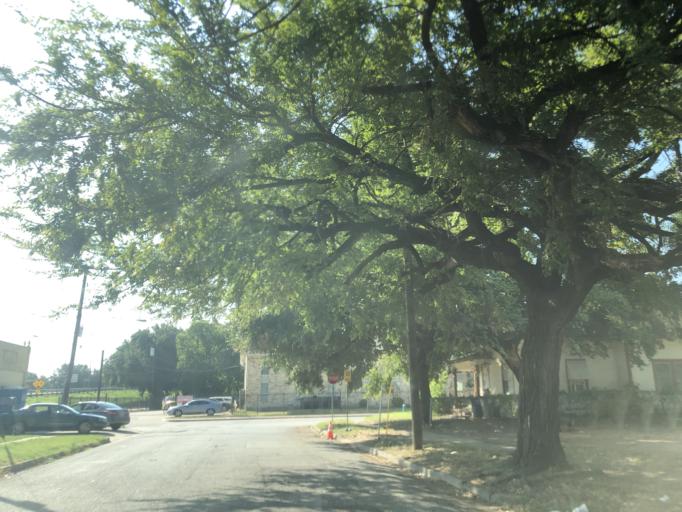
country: US
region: Texas
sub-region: Dallas County
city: Dallas
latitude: 32.7594
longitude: -96.7705
